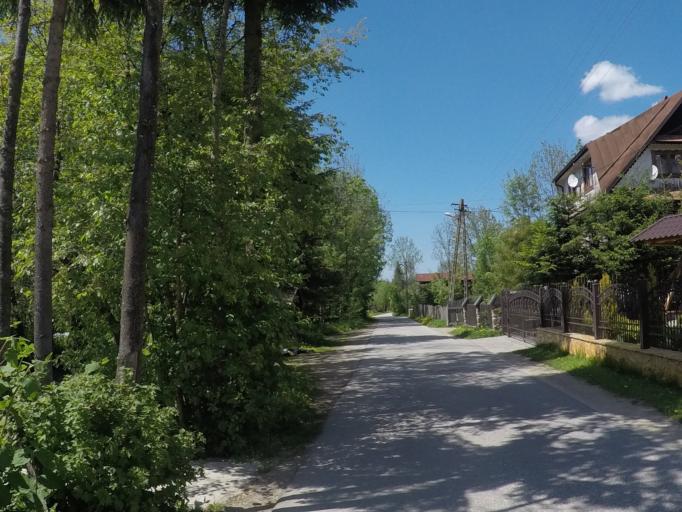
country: PL
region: Lesser Poland Voivodeship
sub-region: Powiat tatrzanski
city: Bukowina Tatrzanska
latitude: 49.3352
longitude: 20.1415
